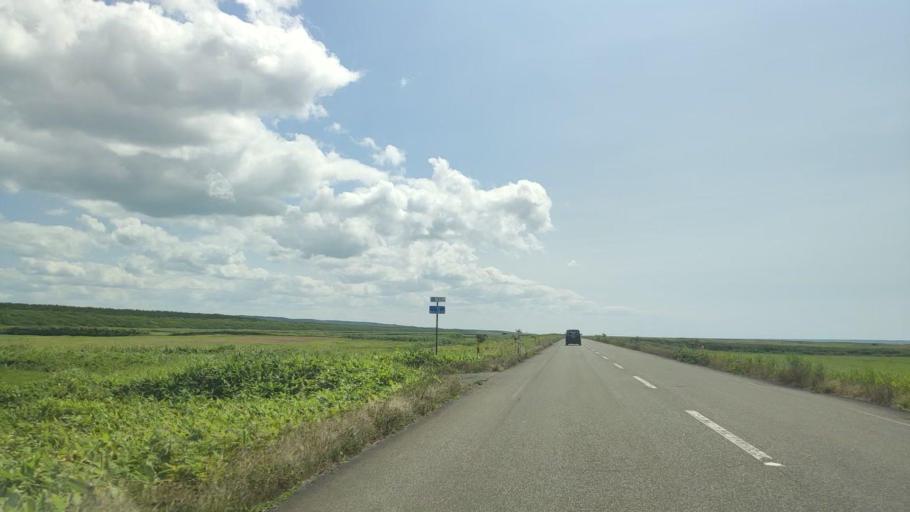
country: JP
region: Hokkaido
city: Wakkanai
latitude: 45.1350
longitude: 141.6037
